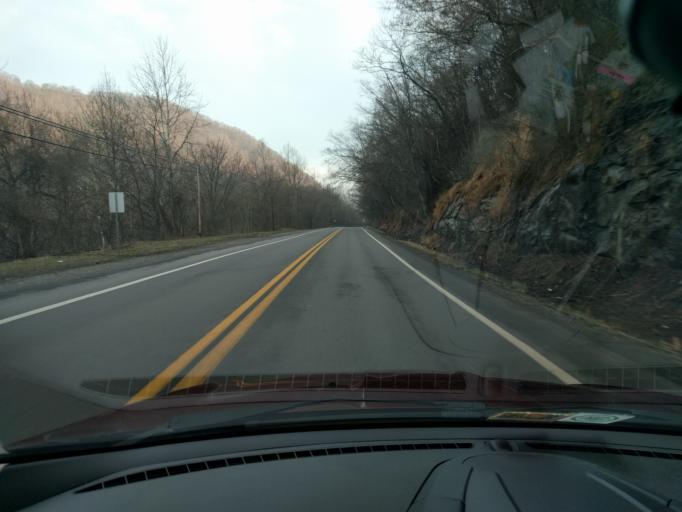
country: US
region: West Virginia
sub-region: Kanawha County
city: Montgomery
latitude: 38.1633
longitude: -81.3017
